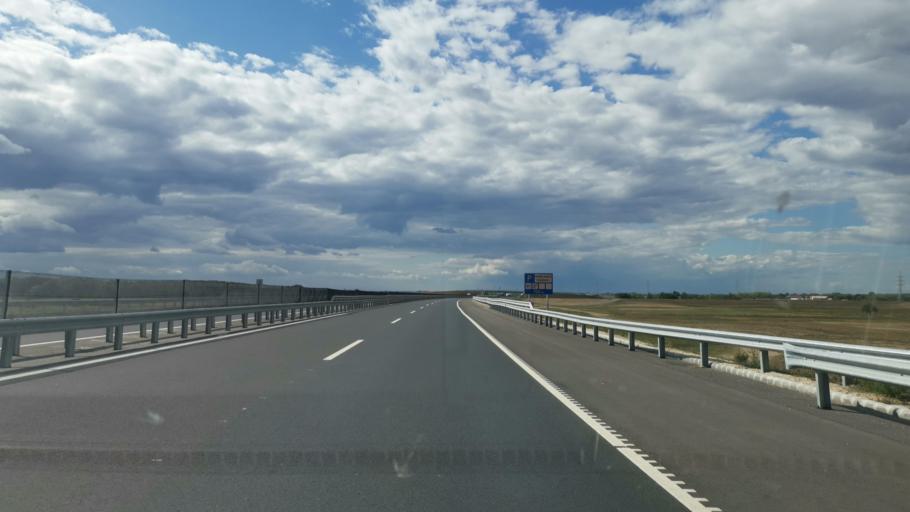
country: HU
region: Jasz-Nagykun-Szolnok
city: Szajol
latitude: 47.2100
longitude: 20.2870
